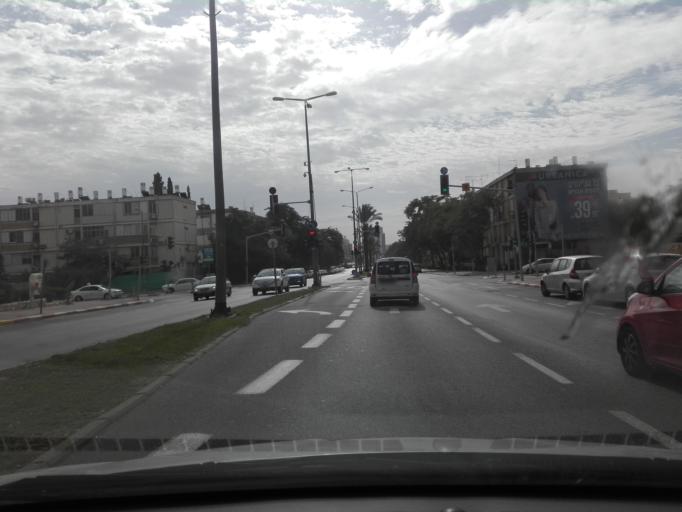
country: IL
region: Southern District
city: Beersheba
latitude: 31.2666
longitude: 34.7981
